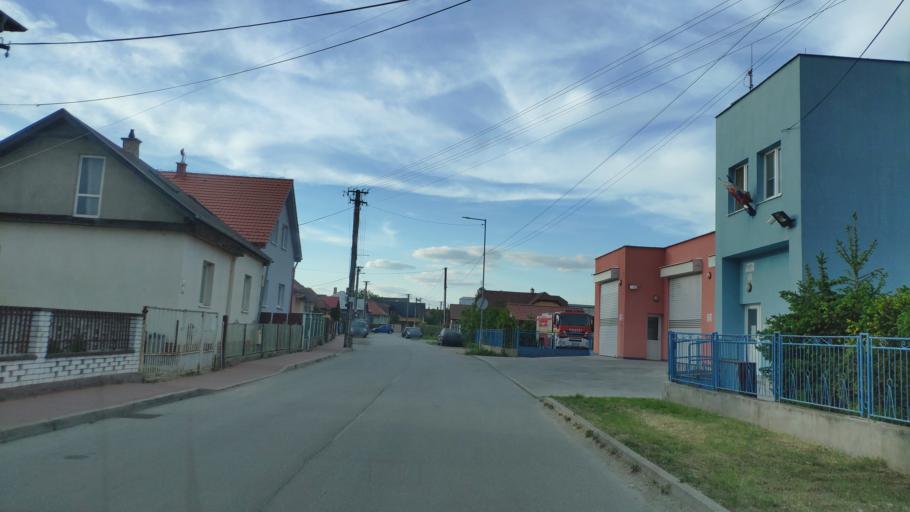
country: SK
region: Kosicky
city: Kosice
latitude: 48.6086
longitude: 21.3258
